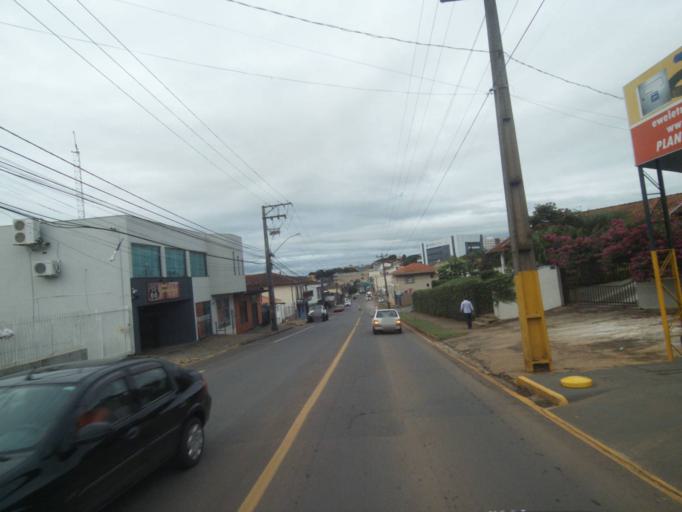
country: BR
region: Parana
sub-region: Telemaco Borba
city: Telemaco Borba
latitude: -24.3342
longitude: -50.6393
